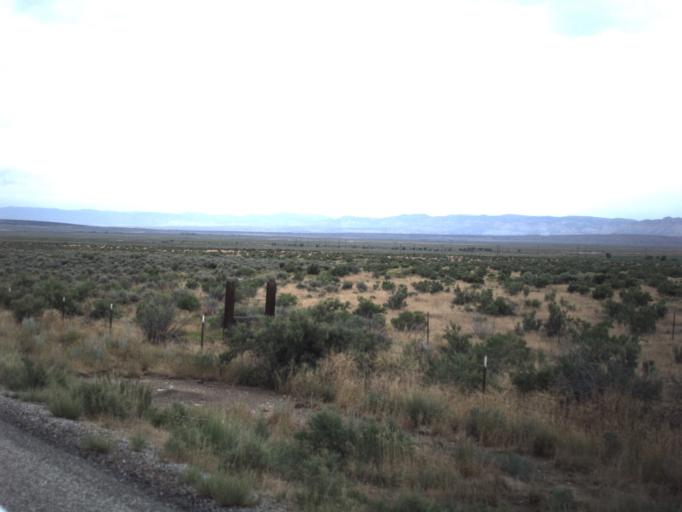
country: US
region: Utah
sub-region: Carbon County
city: East Carbon City
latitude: 39.5360
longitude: -110.4995
